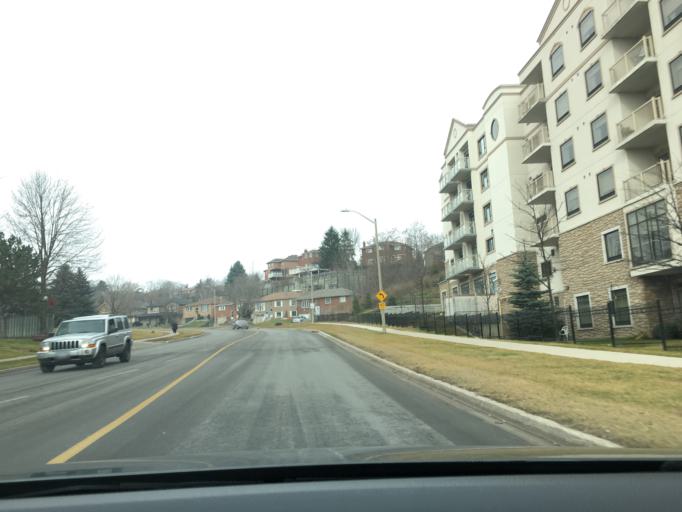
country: CA
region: Ontario
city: Barrie
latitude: 44.3850
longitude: -79.7123
